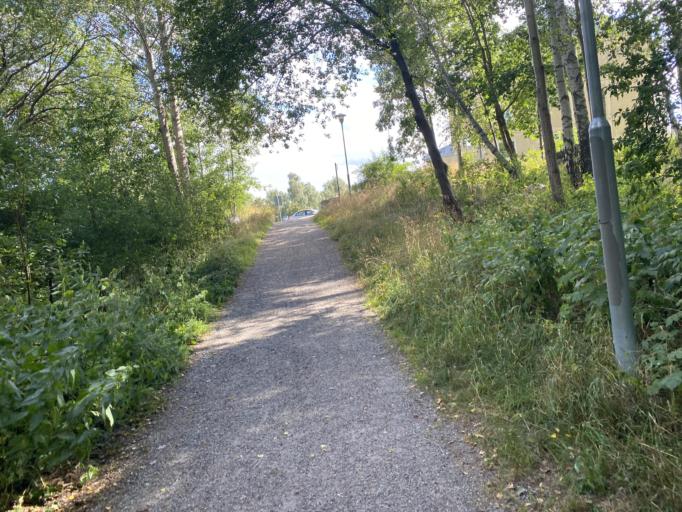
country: SE
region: Stockholm
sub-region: Upplands Vasby Kommun
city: Upplands Vaesby
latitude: 59.4823
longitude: 17.9077
